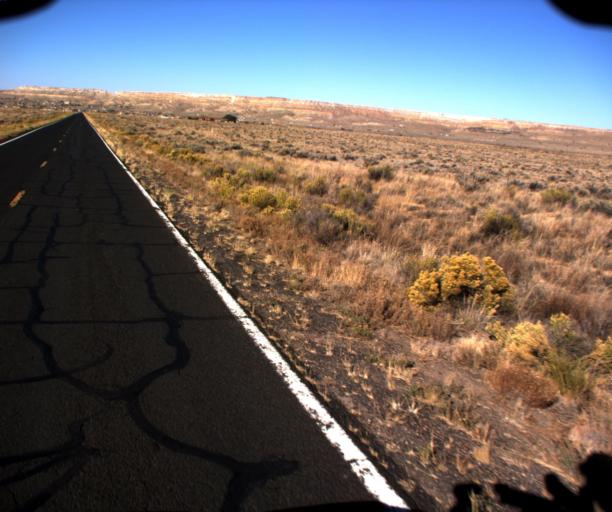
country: US
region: Arizona
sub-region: Navajo County
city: First Mesa
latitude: 35.8415
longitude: -110.3335
